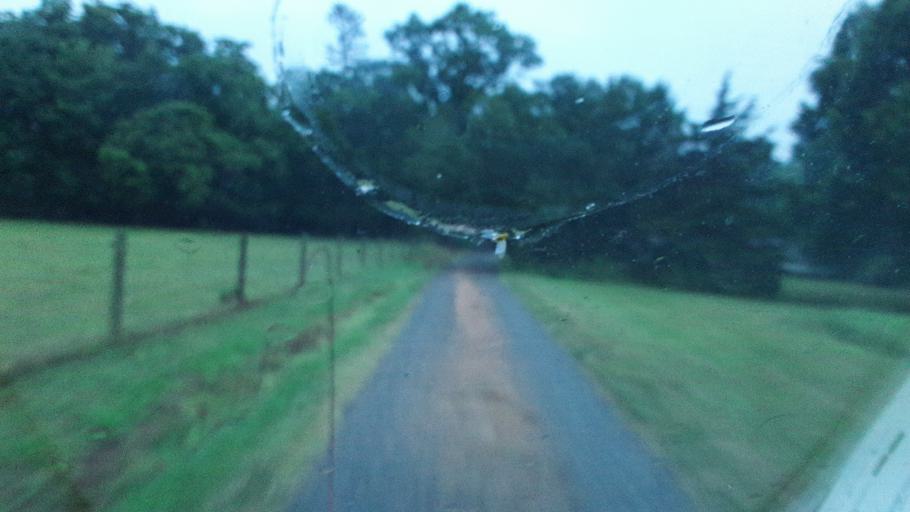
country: US
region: North Carolina
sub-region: Yadkin County
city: Jonesville
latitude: 36.0708
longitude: -80.8367
